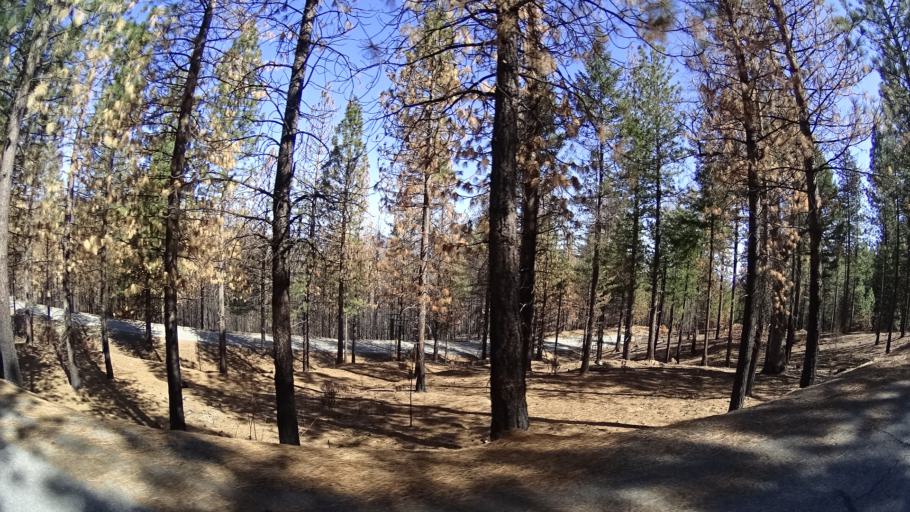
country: US
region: California
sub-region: Tehama County
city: Rancho Tehama Reserve
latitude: 39.6500
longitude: -122.7376
